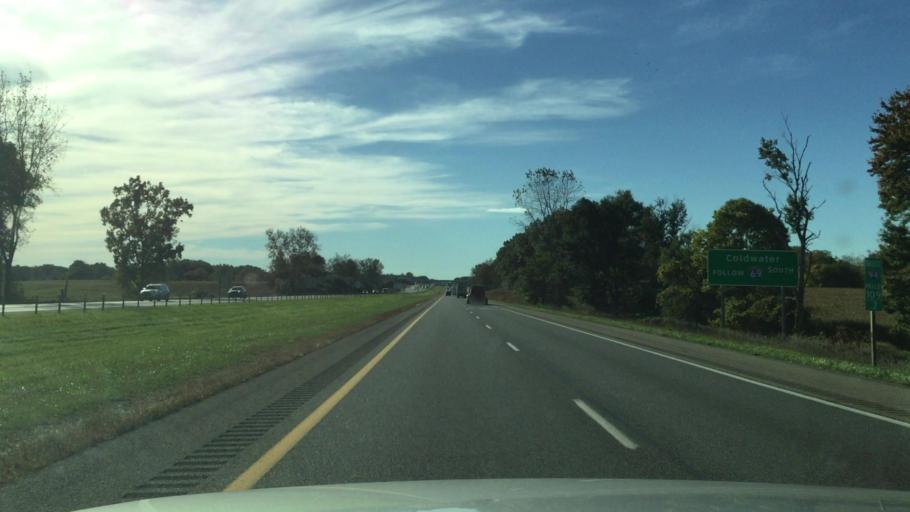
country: US
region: Michigan
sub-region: Calhoun County
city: Marshall
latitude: 42.2973
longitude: -84.9775
